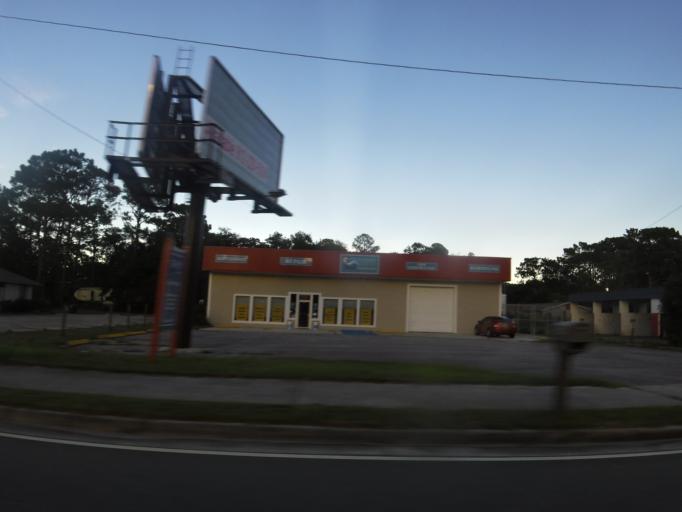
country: US
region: Georgia
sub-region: Camden County
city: St Marys
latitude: 30.7583
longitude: -81.5762
